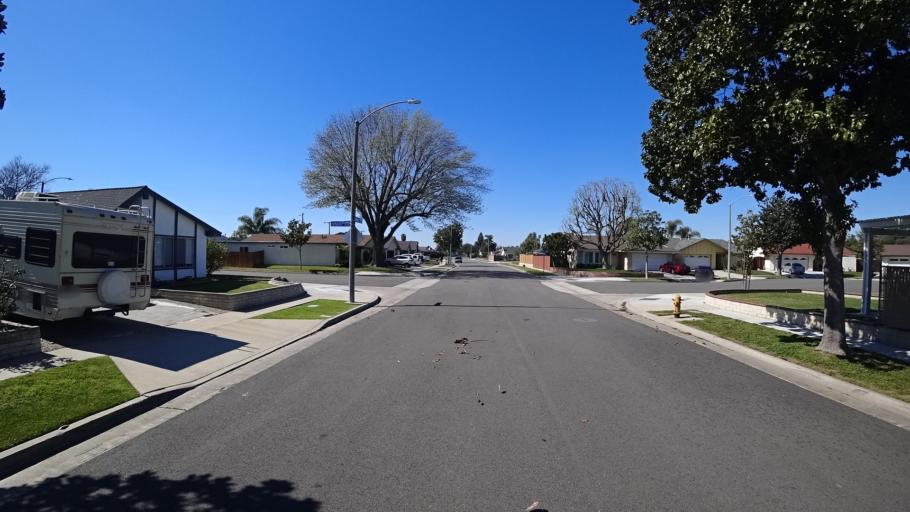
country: US
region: California
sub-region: Orange County
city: Yorba Linda
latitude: 33.8682
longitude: -117.8055
